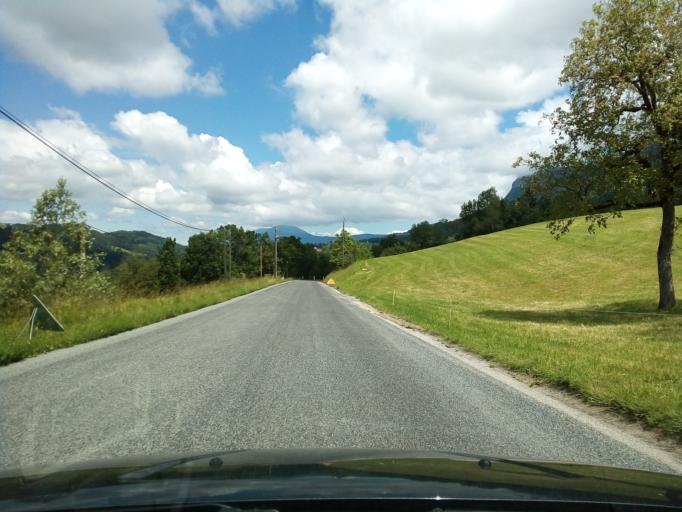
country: FR
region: Rhone-Alpes
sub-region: Departement de la Savoie
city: Les Echelles
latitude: 45.4676
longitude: 5.7565
